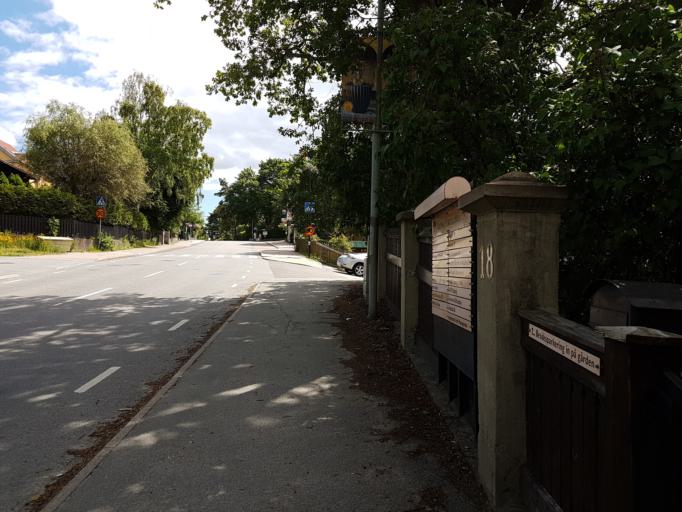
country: SE
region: Stockholm
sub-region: Lidingo
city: Lidingoe
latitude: 59.3608
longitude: 18.1202
